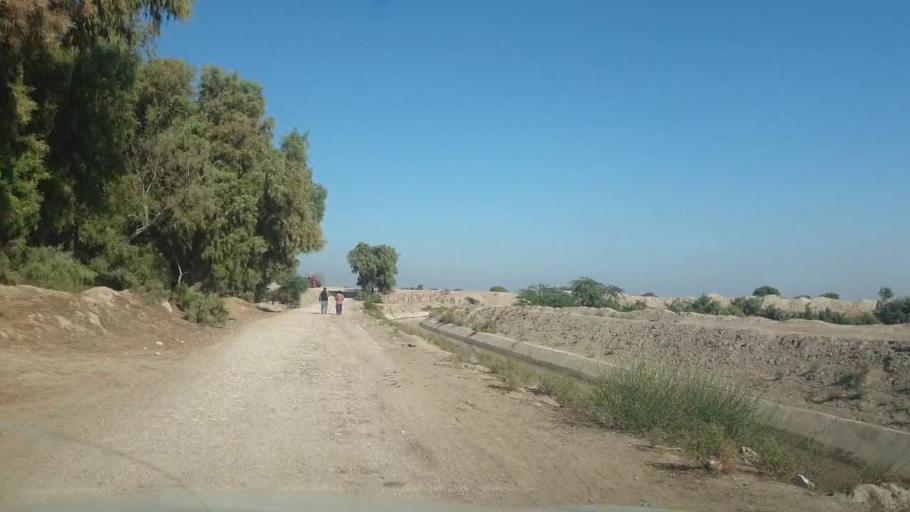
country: PK
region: Sindh
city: Bhan
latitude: 26.5610
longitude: 67.6299
